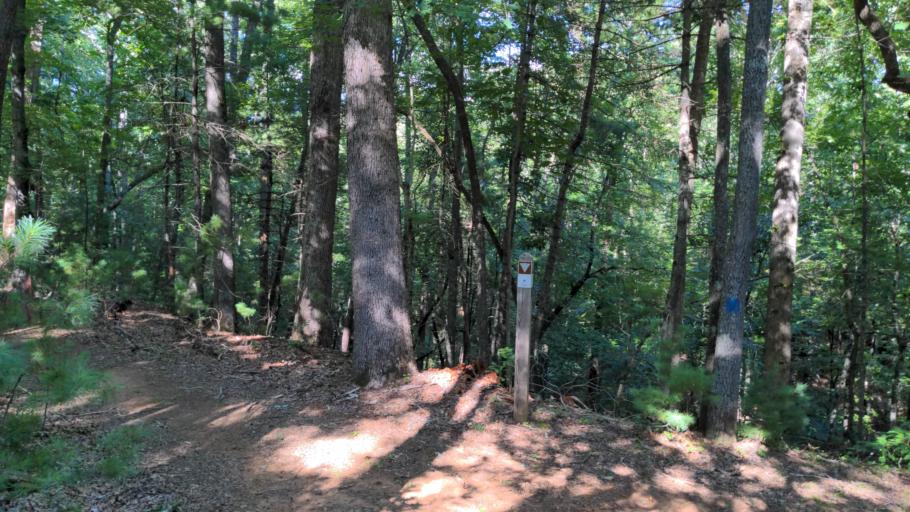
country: US
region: Virginia
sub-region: Henry County
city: Bassett
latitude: 36.7941
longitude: -80.1056
